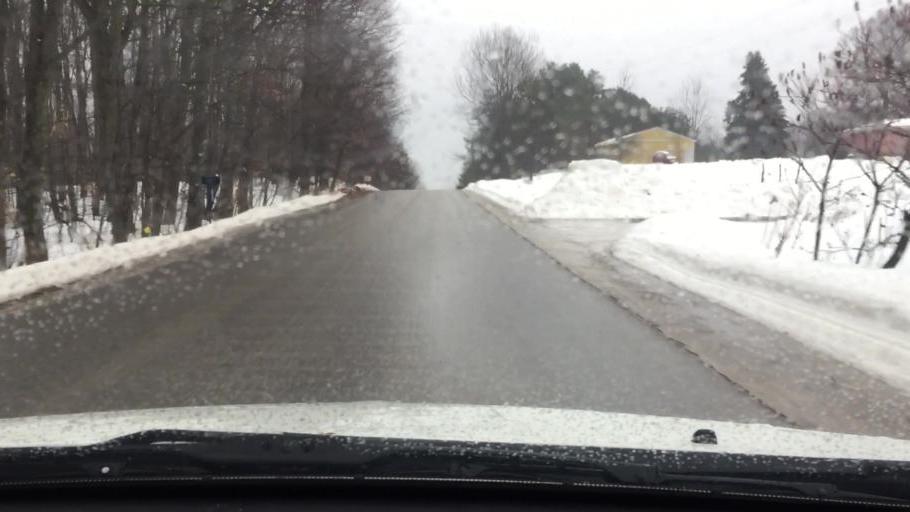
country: US
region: Michigan
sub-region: Charlevoix County
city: East Jordan
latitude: 45.1057
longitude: -85.1574
